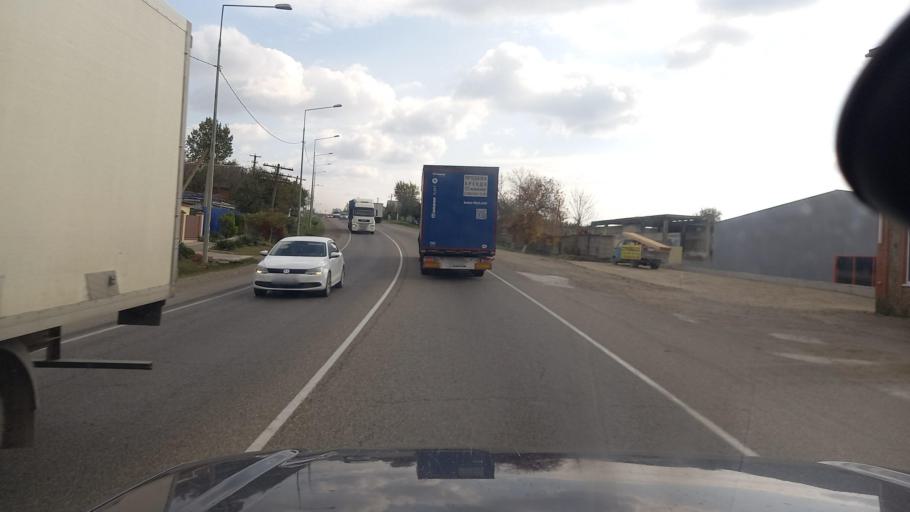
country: RU
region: Krasnodarskiy
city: Kholmskiy
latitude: 44.8488
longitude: 38.4048
